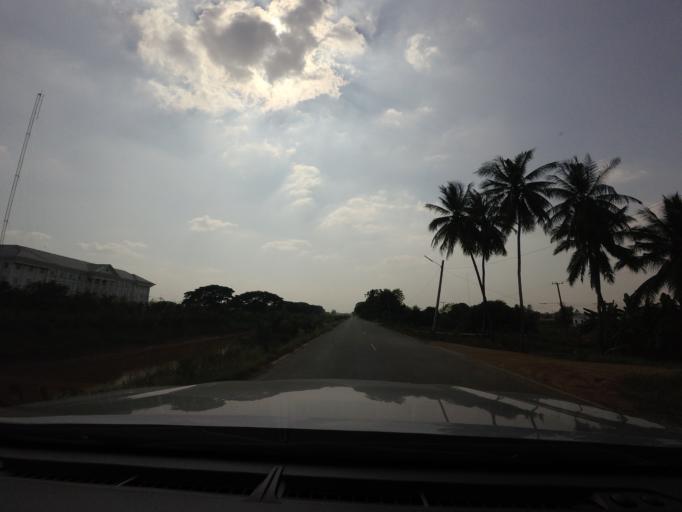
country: TH
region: Phitsanulok
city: Phitsanulok
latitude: 16.7896
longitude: 100.2040
